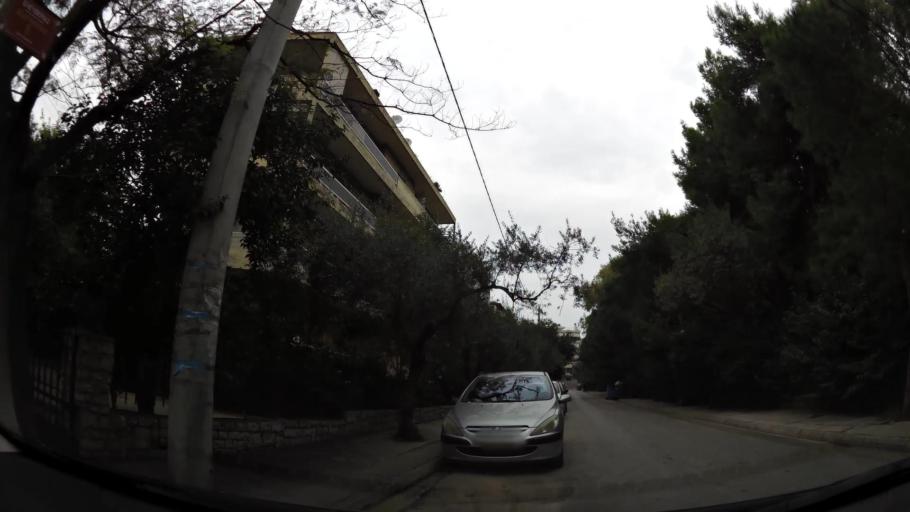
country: GR
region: Attica
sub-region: Nomarchia Athinas
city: Filothei
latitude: 38.0295
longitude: 23.7832
